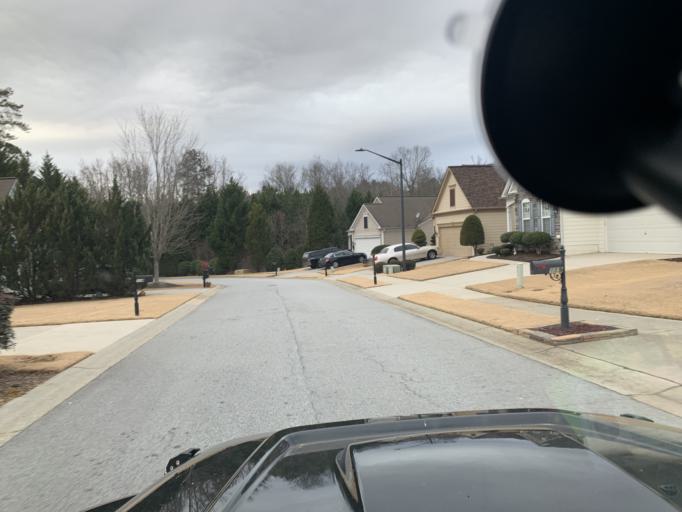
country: US
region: Georgia
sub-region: Cherokee County
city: Woodstock
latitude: 34.0874
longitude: -84.4562
